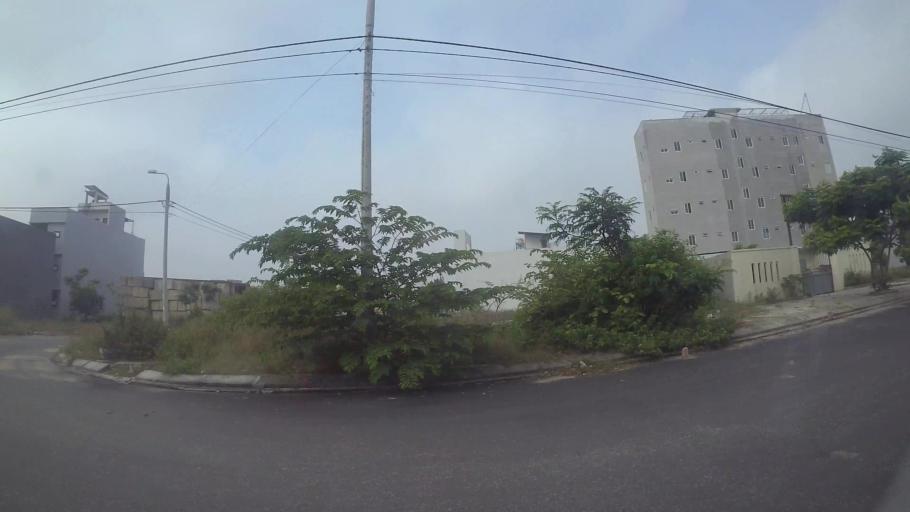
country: VN
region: Da Nang
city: Ngu Hanh Son
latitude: 16.0206
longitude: 108.2469
